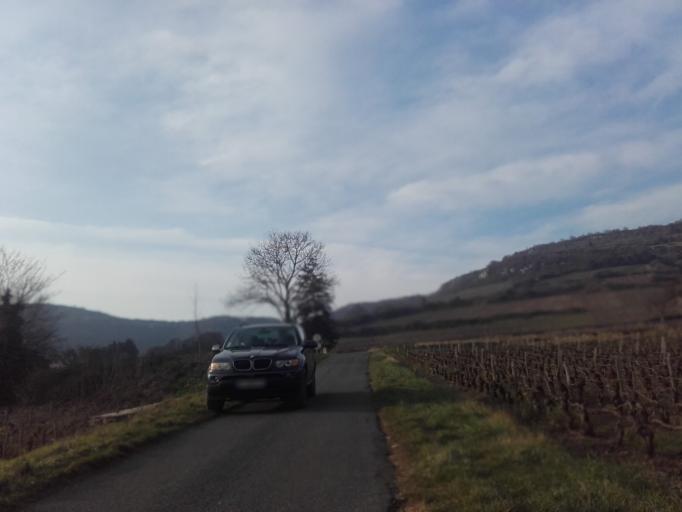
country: FR
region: Bourgogne
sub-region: Departement de Saone-et-Loire
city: Chagny
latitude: 46.9140
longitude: 4.6878
